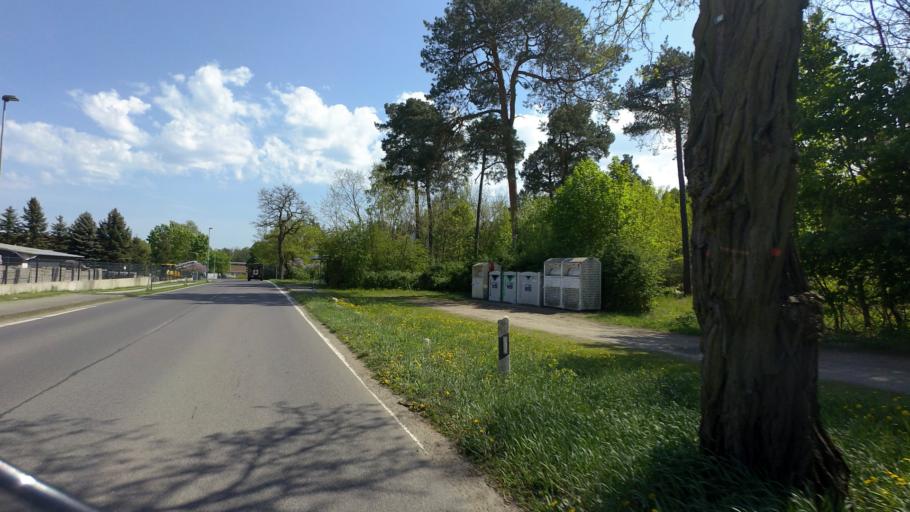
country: DE
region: Brandenburg
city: Lieberose
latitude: 51.9807
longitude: 14.2885
